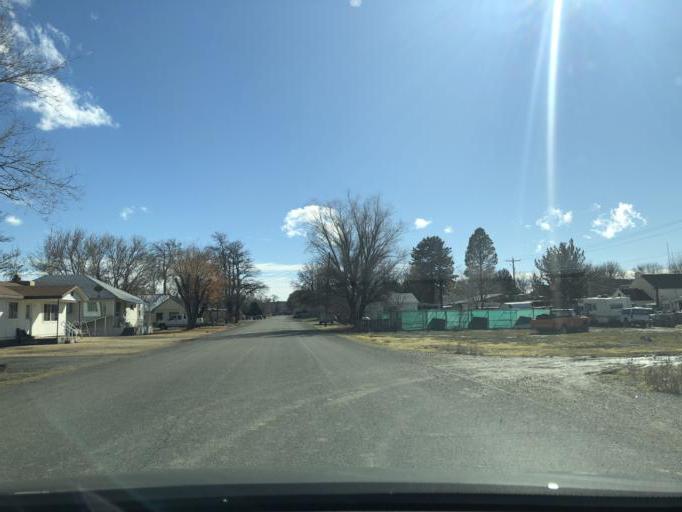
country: US
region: Utah
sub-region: Carbon County
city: East Carbon City
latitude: 38.9950
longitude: -110.1610
